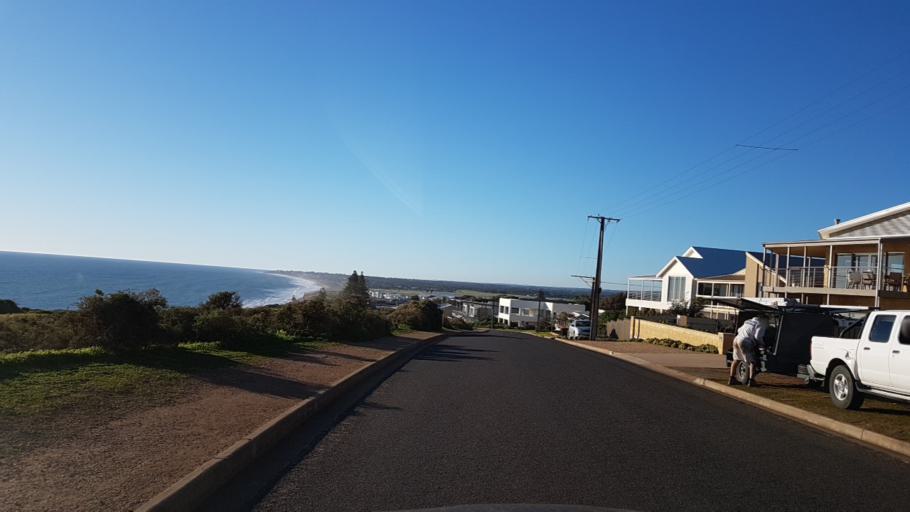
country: AU
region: South Australia
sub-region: Onkaparinga
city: Port Willunga
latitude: -35.3349
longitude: 138.4481
